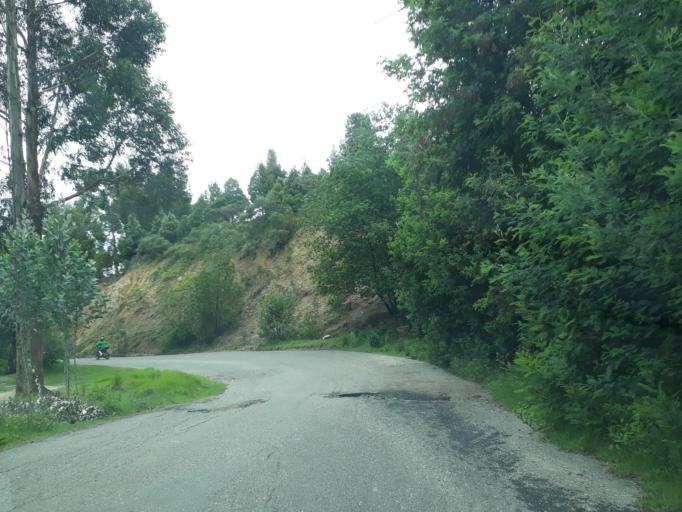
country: CO
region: Cundinamarca
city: Cucunuba
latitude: 5.2242
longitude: -73.7801
